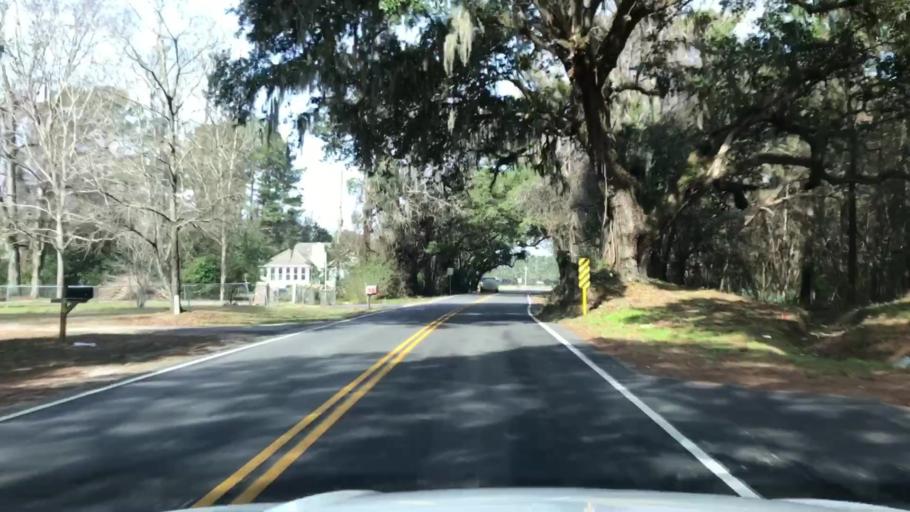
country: US
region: South Carolina
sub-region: Charleston County
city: Folly Beach
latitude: 32.7173
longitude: -80.0208
